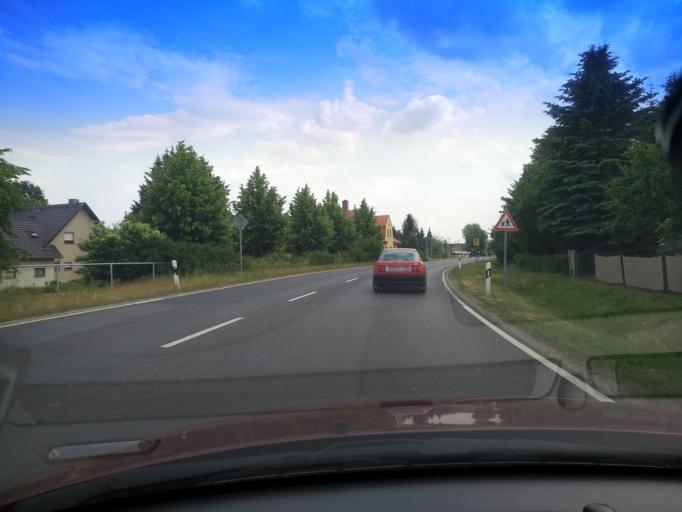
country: DE
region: Saxony
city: Kodersdorf
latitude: 51.2460
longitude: 14.8889
